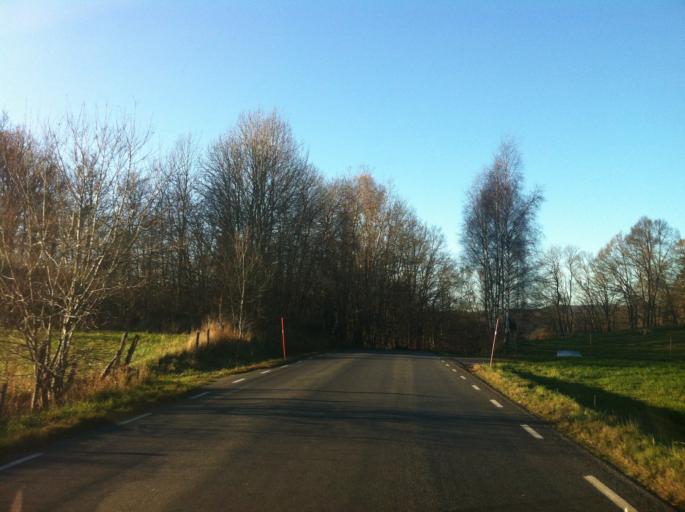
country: SE
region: Blekinge
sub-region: Olofstroms Kommun
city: Jamshog
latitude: 56.1810
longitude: 14.5678
